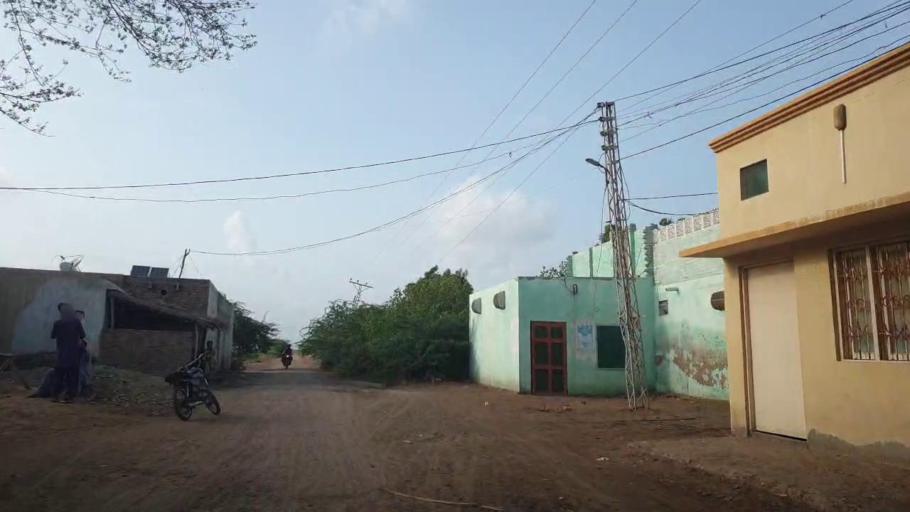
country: PK
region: Sindh
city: Tando Bago
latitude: 24.6459
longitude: 69.1118
